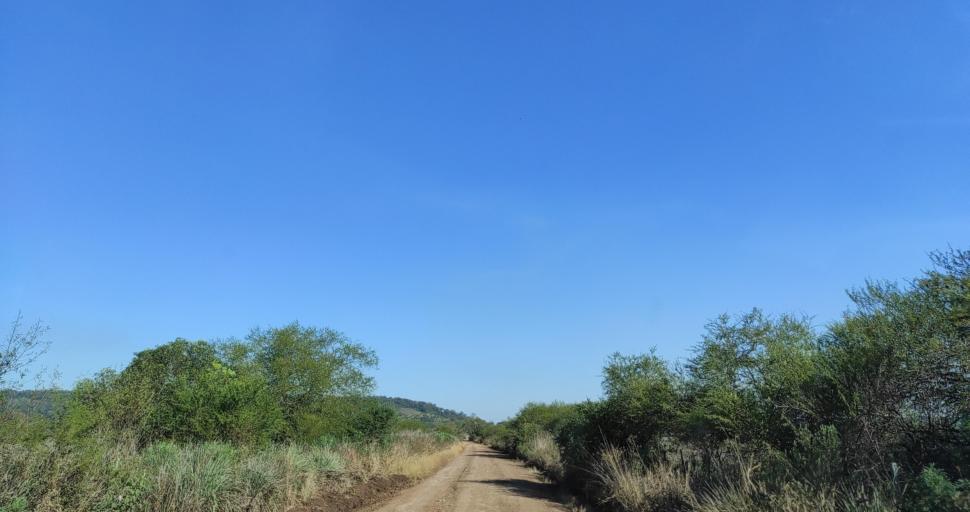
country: AR
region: Misiones
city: Cerro Cora
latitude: -27.6570
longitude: -55.6586
